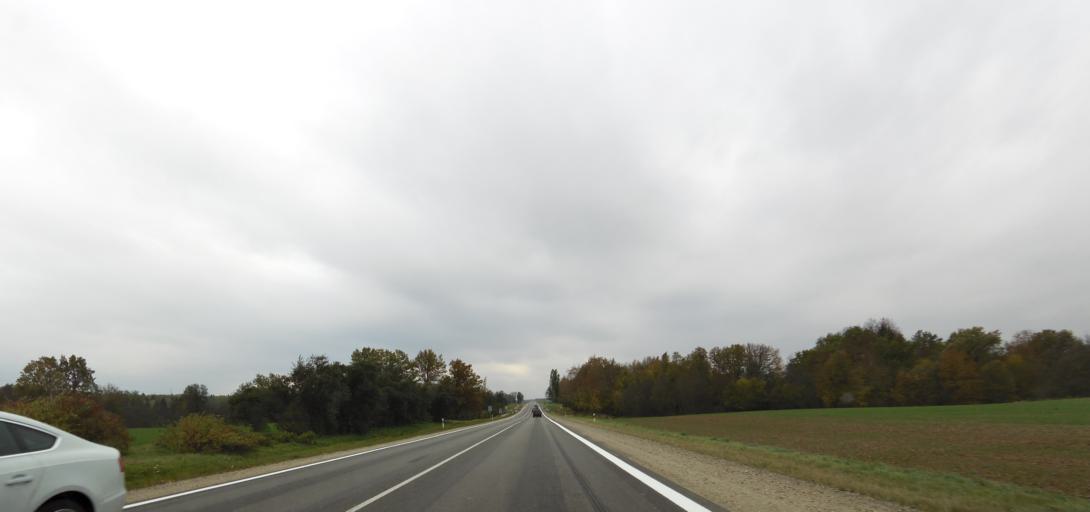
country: LT
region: Panevezys
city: Pasvalys
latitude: 56.1104
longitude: 24.4662
